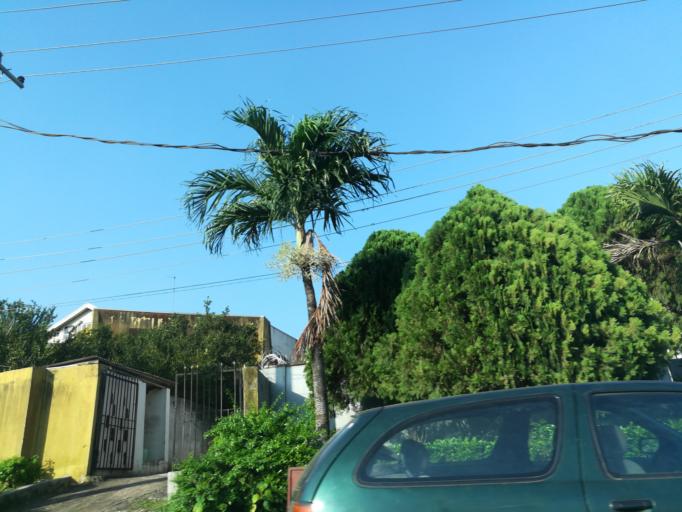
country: NG
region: Lagos
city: Ojota
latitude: 6.5842
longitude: 3.3658
